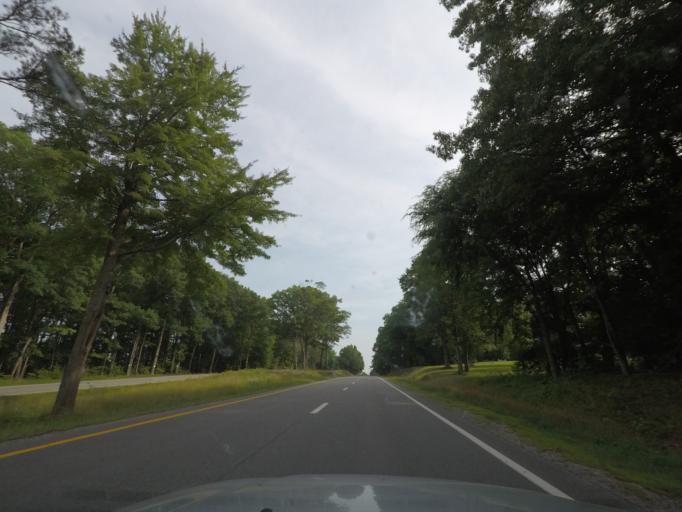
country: US
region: Virginia
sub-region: Charlotte County
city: Charlotte Court House
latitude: 36.9754
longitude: -78.4904
